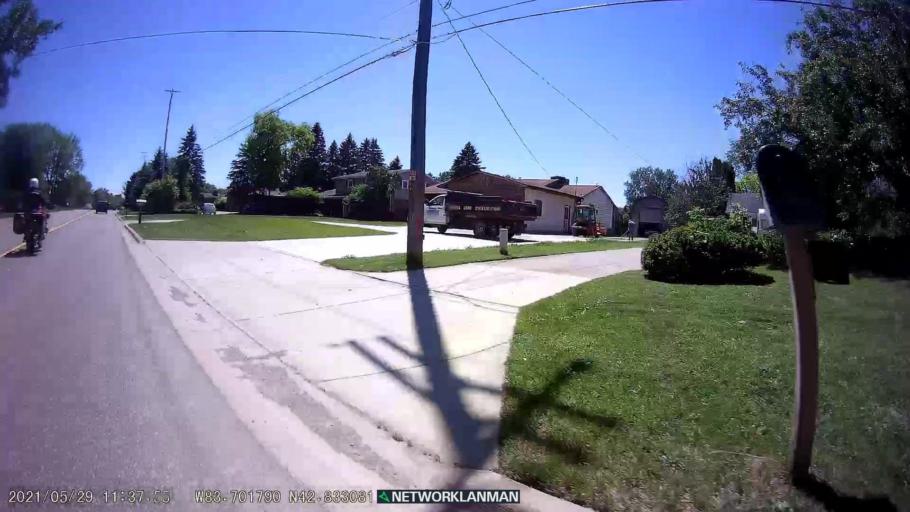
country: US
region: Michigan
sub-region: Genesee County
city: Lake Fenton
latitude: 42.8328
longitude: -83.7018
